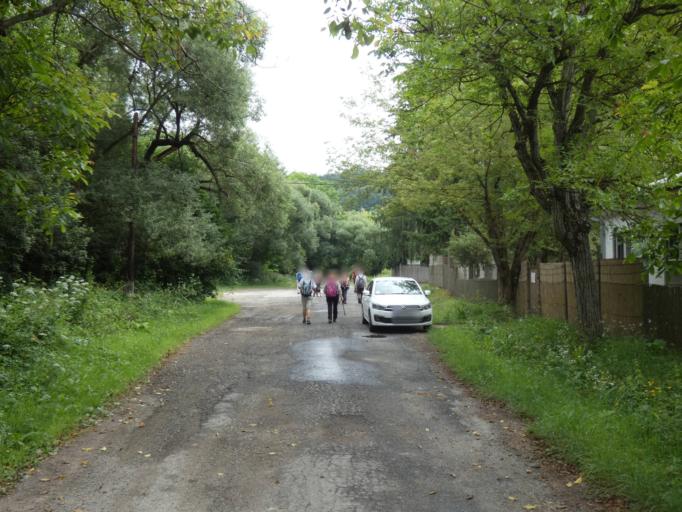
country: HU
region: Pest
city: Szob
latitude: 47.8228
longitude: 18.8999
